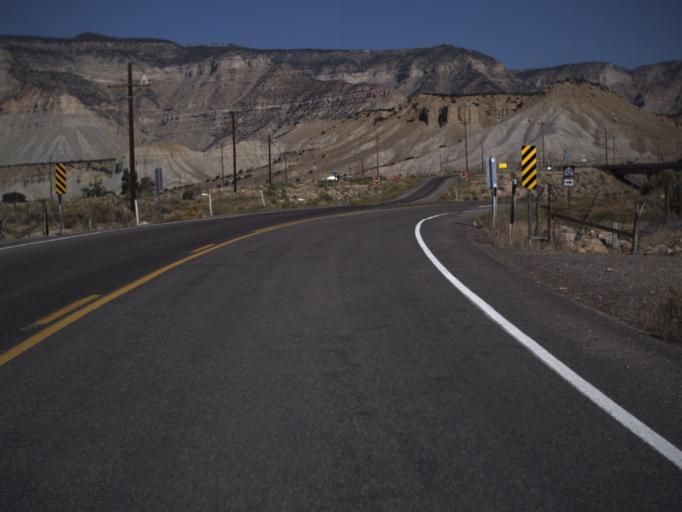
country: US
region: Utah
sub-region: Emery County
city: Orangeville
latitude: 39.2518
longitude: -111.0970
